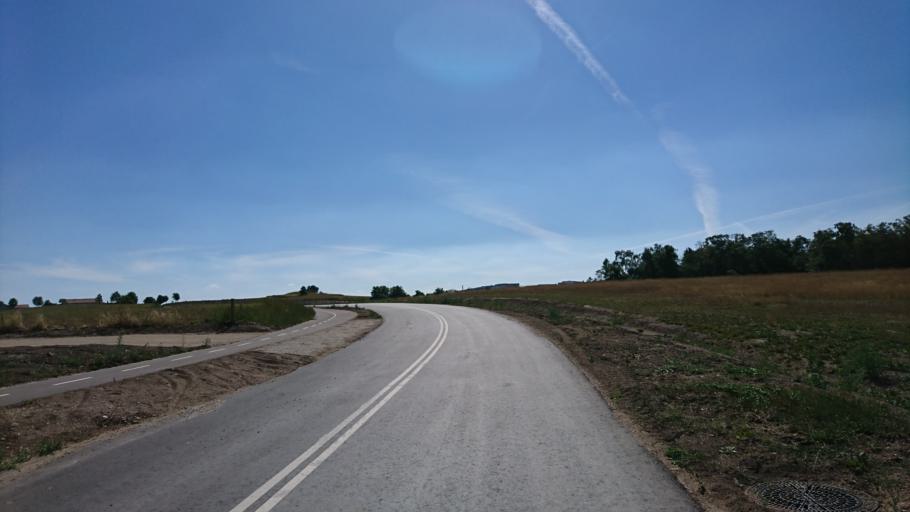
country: DK
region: Capital Region
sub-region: Ballerup Kommune
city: Malov
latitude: 55.7604
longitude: 12.3097
